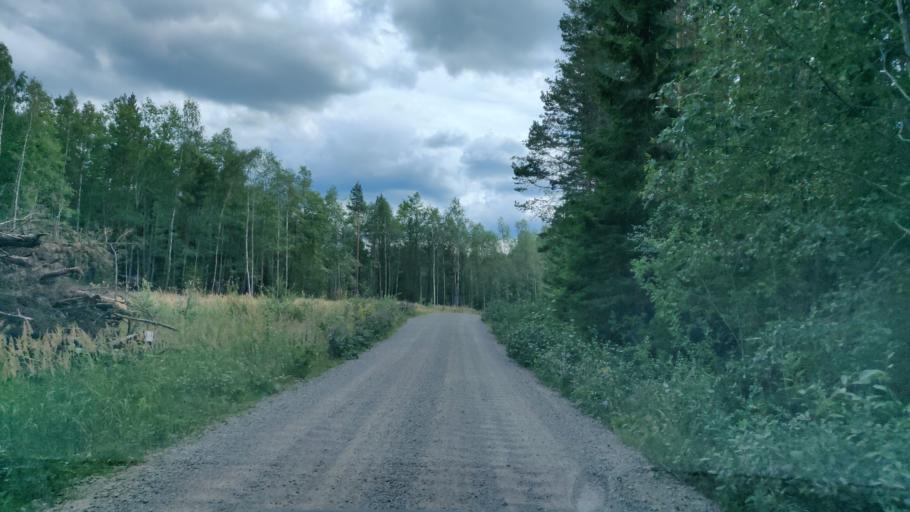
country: SE
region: Vaermland
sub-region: Hagfors Kommun
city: Hagfors
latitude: 60.0127
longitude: 13.7061
